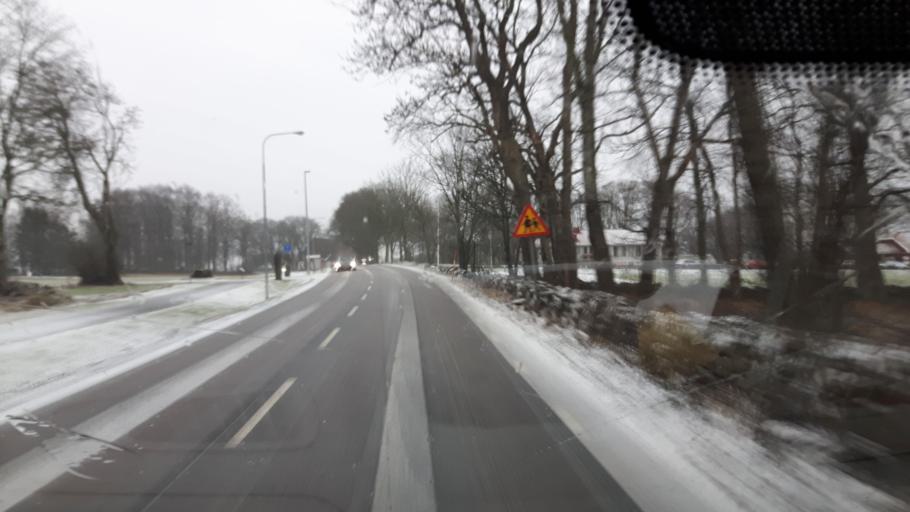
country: SE
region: Halland
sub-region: Kungsbacka Kommun
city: Vallda
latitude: 57.4810
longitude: 12.0059
